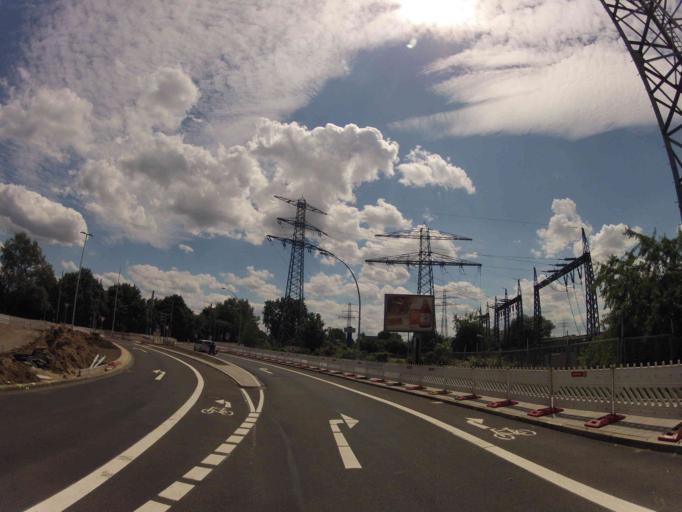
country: DE
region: Hamburg
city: Rothenburgsort
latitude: 53.5269
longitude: 10.0691
